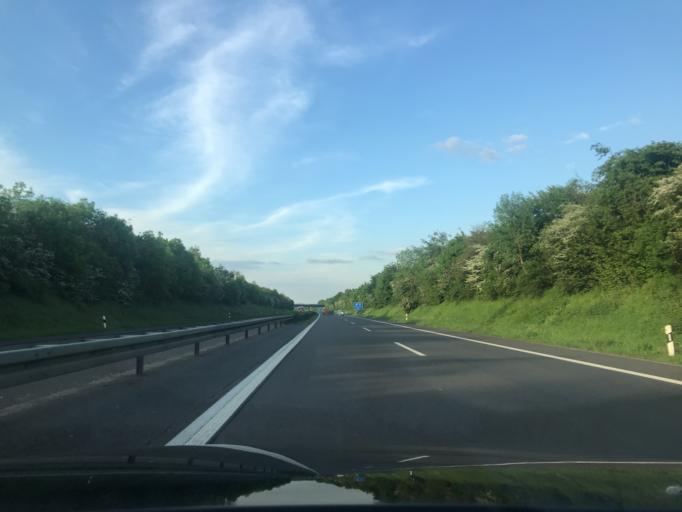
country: DE
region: North Rhine-Westphalia
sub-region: Regierungsbezirk Koln
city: Heinsberg
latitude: 51.0346
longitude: 6.1499
